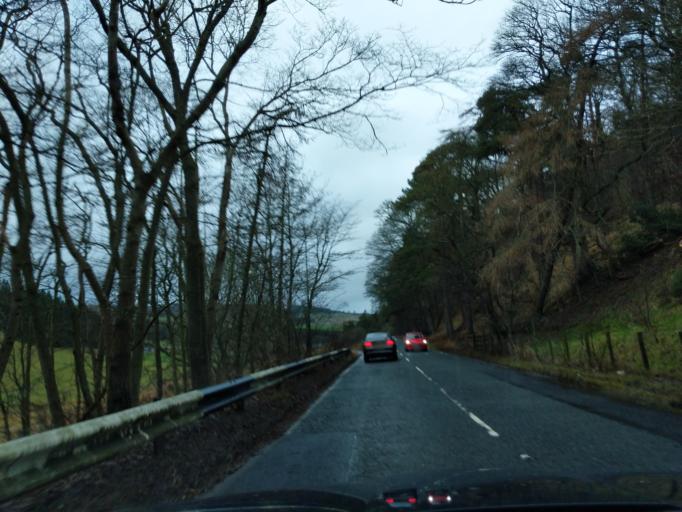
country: GB
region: Scotland
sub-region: The Scottish Borders
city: Galashiels
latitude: 55.6460
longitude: -2.8559
